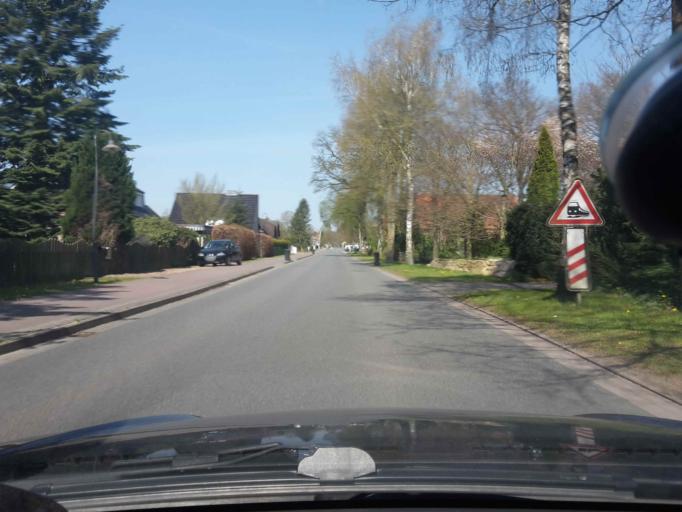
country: DE
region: Lower Saxony
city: Handeloh
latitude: 53.2415
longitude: 9.8481
